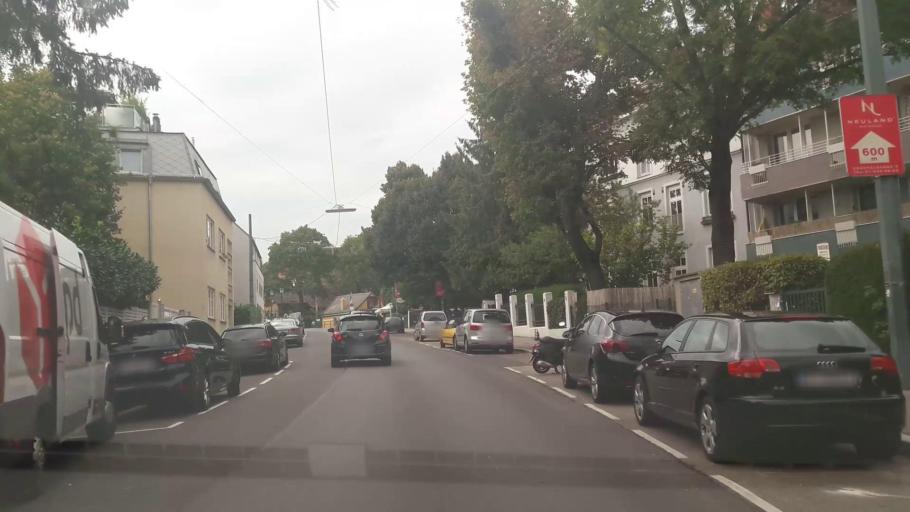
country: AT
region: Lower Austria
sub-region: Politischer Bezirk Korneuburg
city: Langenzersdorf
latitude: 48.2553
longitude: 16.3461
